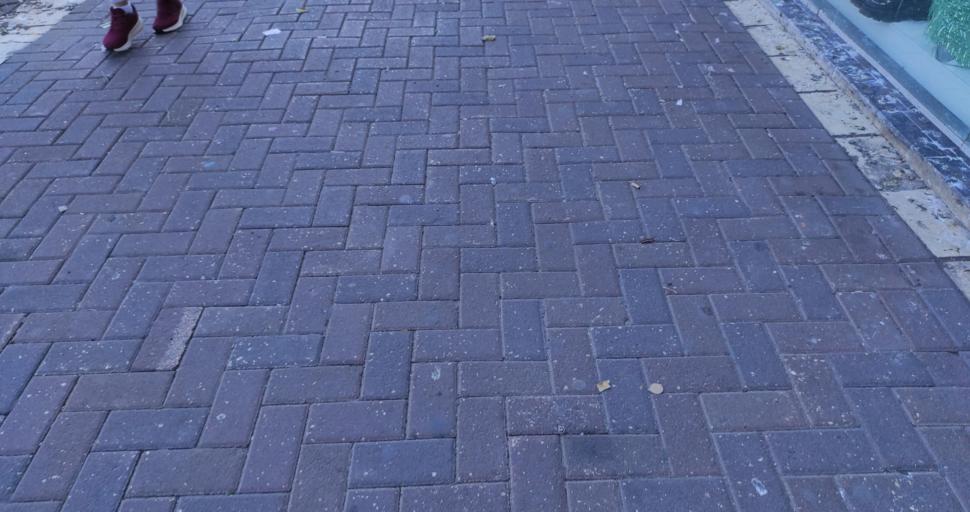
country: IL
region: Central District
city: Netanya
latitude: 32.3279
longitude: 34.8581
